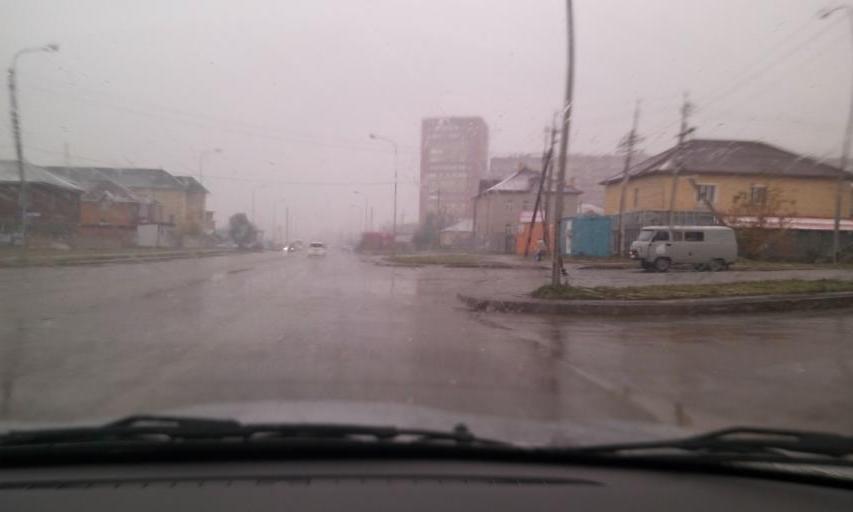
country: KZ
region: Astana Qalasy
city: Astana
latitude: 51.1782
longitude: 71.3703
